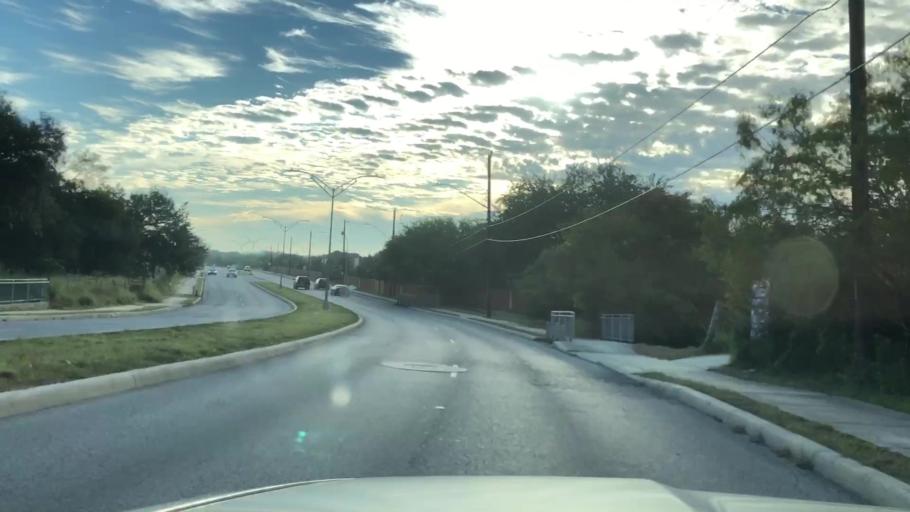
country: US
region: Texas
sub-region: Bexar County
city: Leon Valley
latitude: 29.5416
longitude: -98.6358
